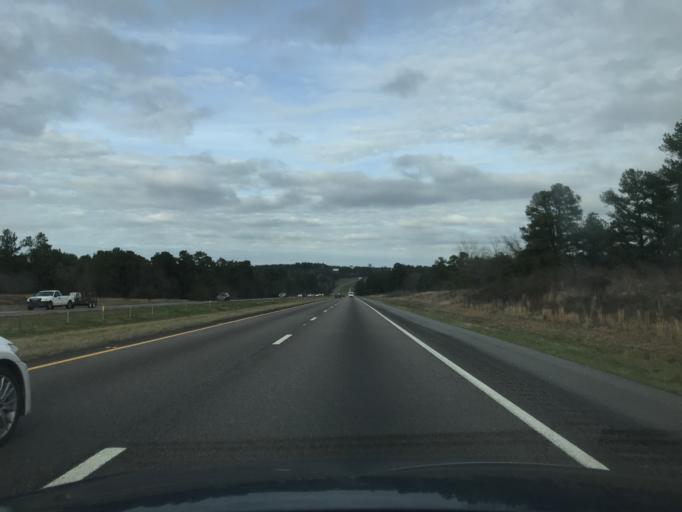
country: US
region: South Carolina
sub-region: Edgefield County
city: Murphys Estates
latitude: 33.5919
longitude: -81.8770
